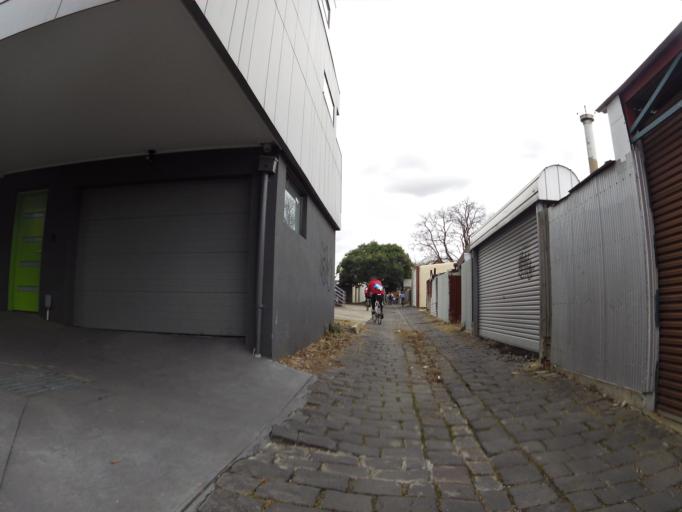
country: AU
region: Victoria
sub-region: Moonee Valley
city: Moonee Ponds
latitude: -37.7612
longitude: 144.9265
